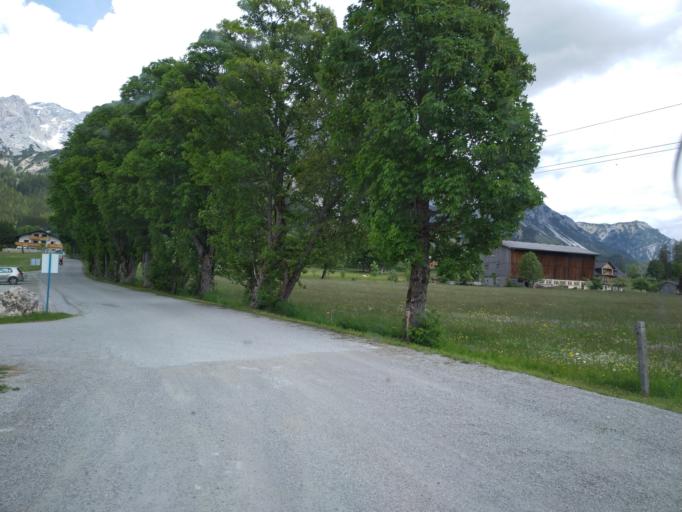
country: AT
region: Styria
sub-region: Politischer Bezirk Liezen
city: Schladming
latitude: 47.4236
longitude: 13.6247
